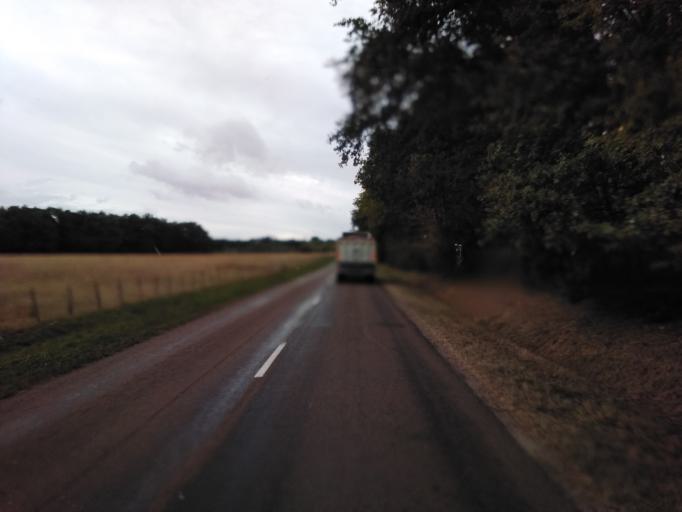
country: FR
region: Champagne-Ardenne
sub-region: Departement de l'Aube
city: Brienne-le-Chateau
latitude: 48.3103
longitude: 4.5219
